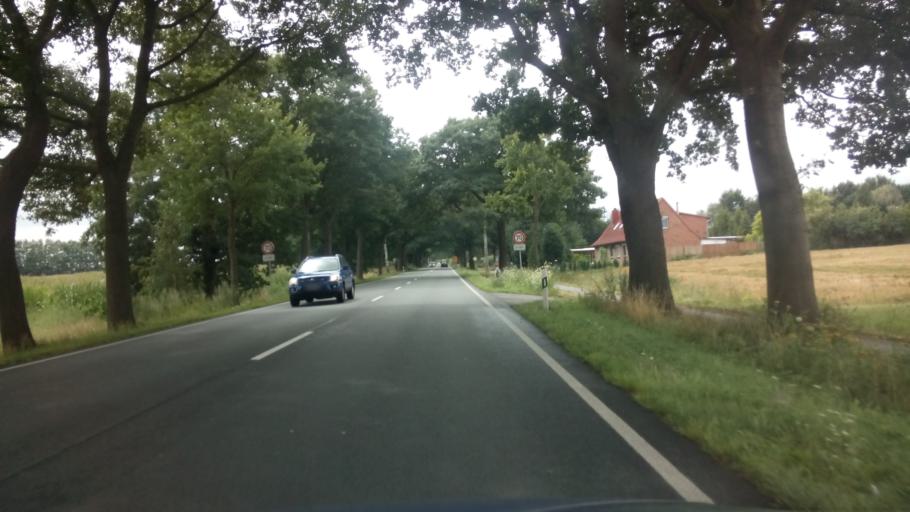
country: DE
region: Lower Saxony
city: Bassum
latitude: 52.8782
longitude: 8.7285
